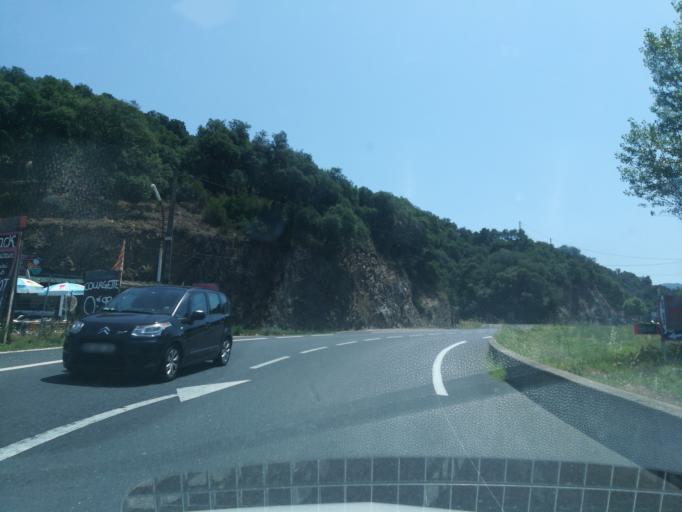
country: FR
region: Languedoc-Roussillon
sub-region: Departement des Pyrenees-Orientales
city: Montesquiu d'Albera
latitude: 42.4733
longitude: 2.8564
